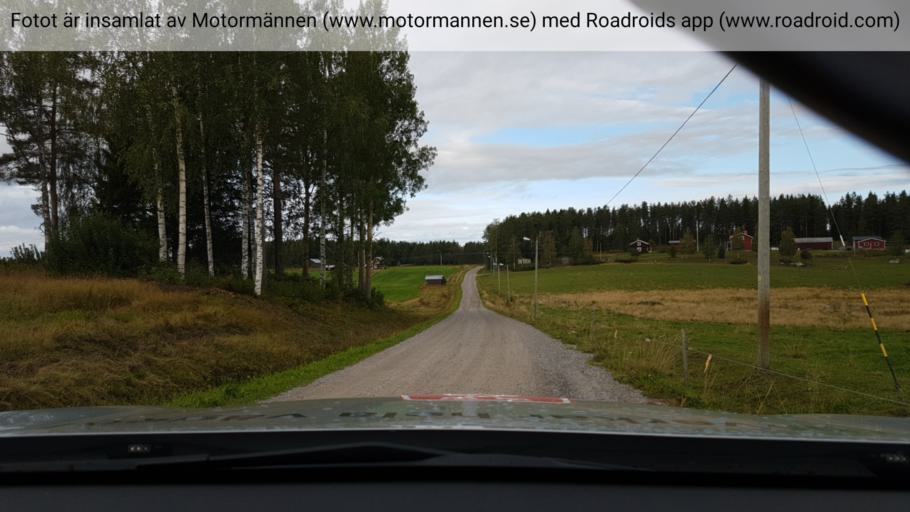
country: SE
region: Vaesterbotten
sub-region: Skelleftea Kommun
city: Byske
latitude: 65.1202
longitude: 21.2112
